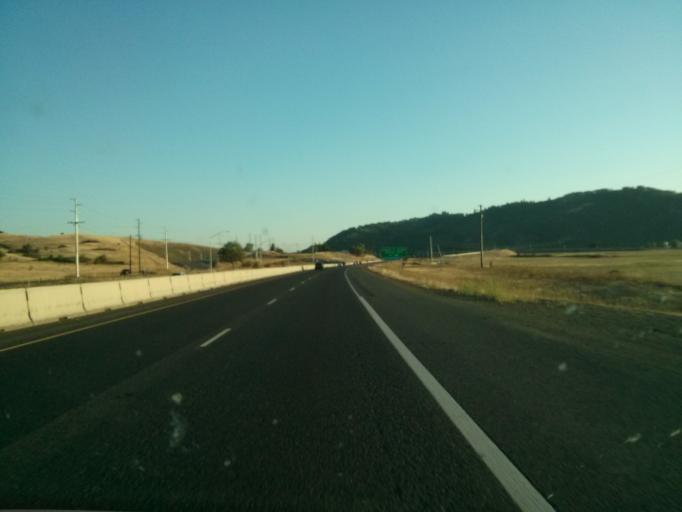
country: US
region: Oregon
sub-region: Douglas County
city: Roseburg North
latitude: 43.2987
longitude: -123.3505
